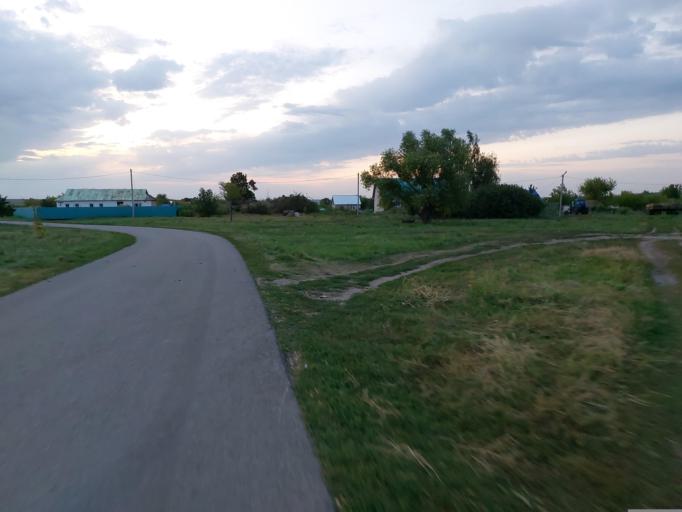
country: RU
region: Lipetsk
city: Dolgorukovo
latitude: 52.3777
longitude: 38.0505
